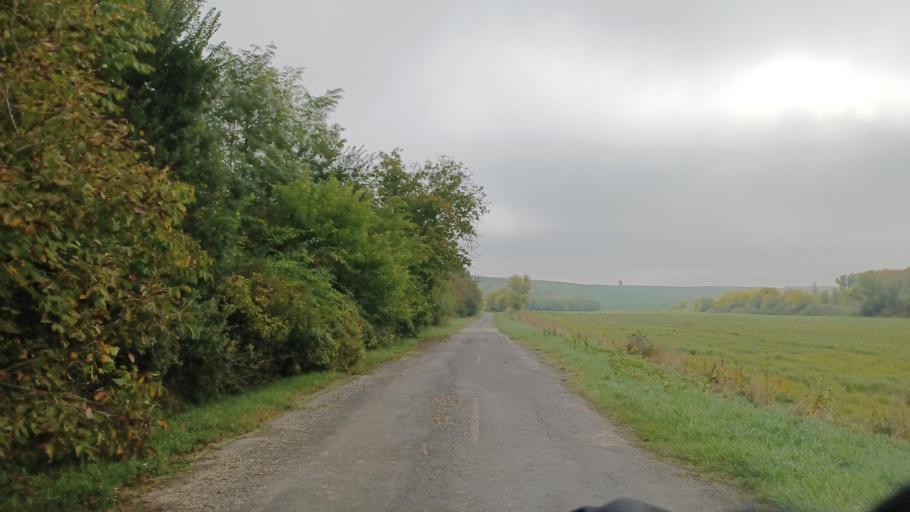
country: HU
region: Tolna
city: Simontornya
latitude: 46.6469
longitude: 18.5433
